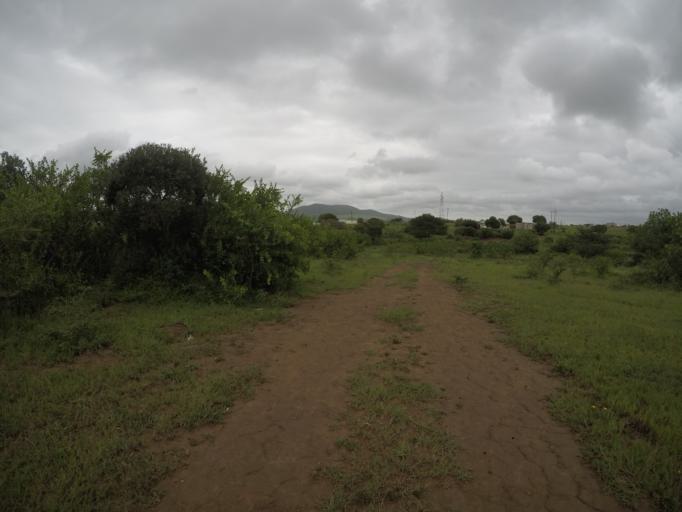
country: ZA
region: KwaZulu-Natal
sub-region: uThungulu District Municipality
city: Empangeni
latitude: -28.6054
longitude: 31.8533
